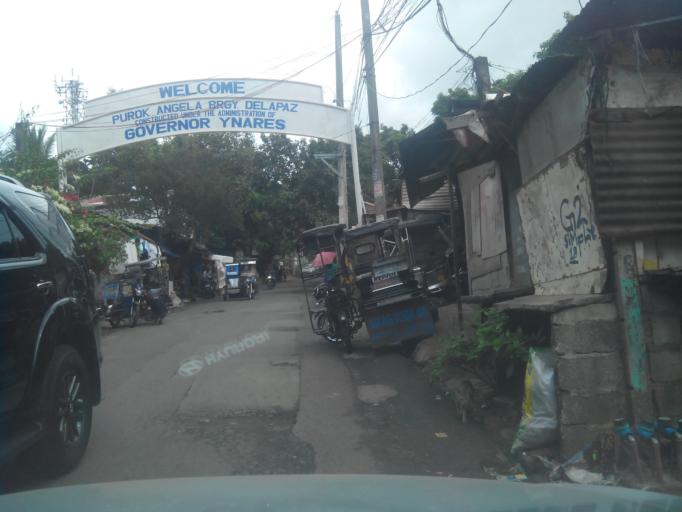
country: PH
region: Calabarzon
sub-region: Province of Rizal
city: Antipolo
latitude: 14.6025
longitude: 121.1761
